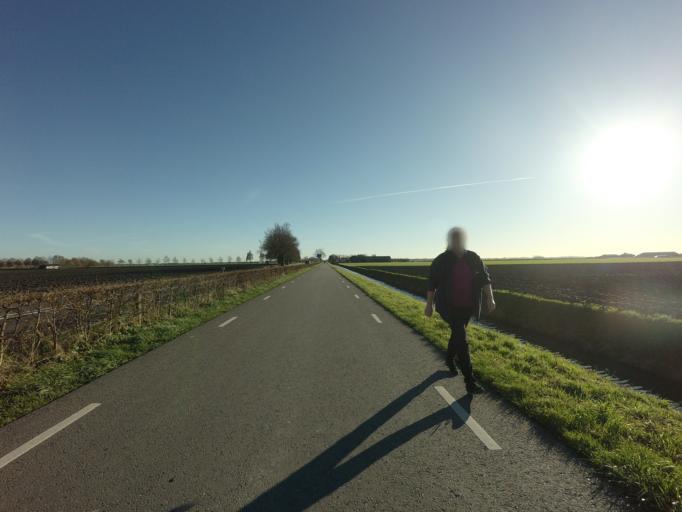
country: NL
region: South Holland
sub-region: Gemeente Nieuwkoop
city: Nieuwkoop
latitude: 52.1799
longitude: 4.7673
